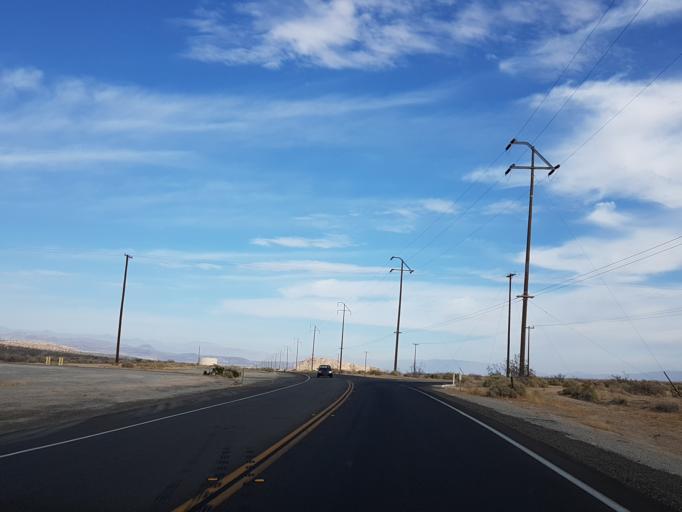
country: US
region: California
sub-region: Kern County
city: Ridgecrest
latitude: 35.6230
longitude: -117.5968
